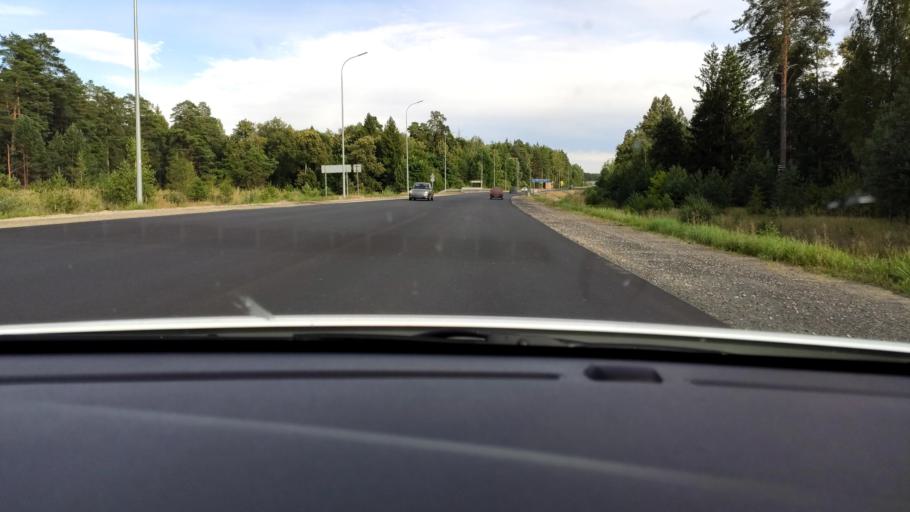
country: RU
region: Mariy-El
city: Yoshkar-Ola
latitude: 56.5406
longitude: 47.9836
